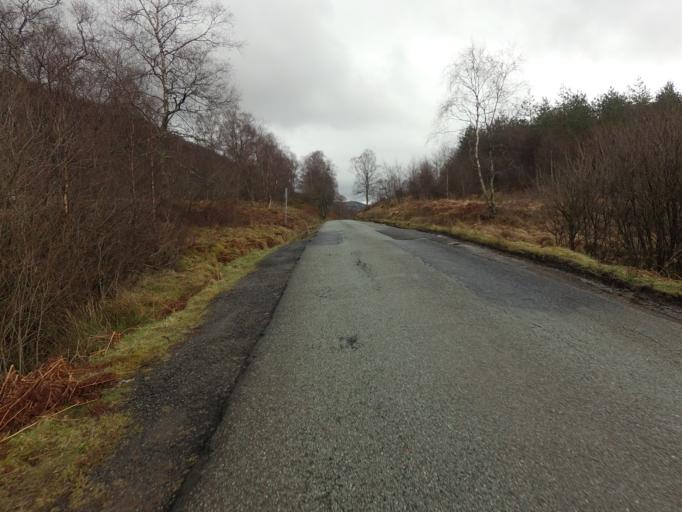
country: GB
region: Scotland
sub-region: West Dunbartonshire
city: Balloch
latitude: 56.2432
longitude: -4.5729
